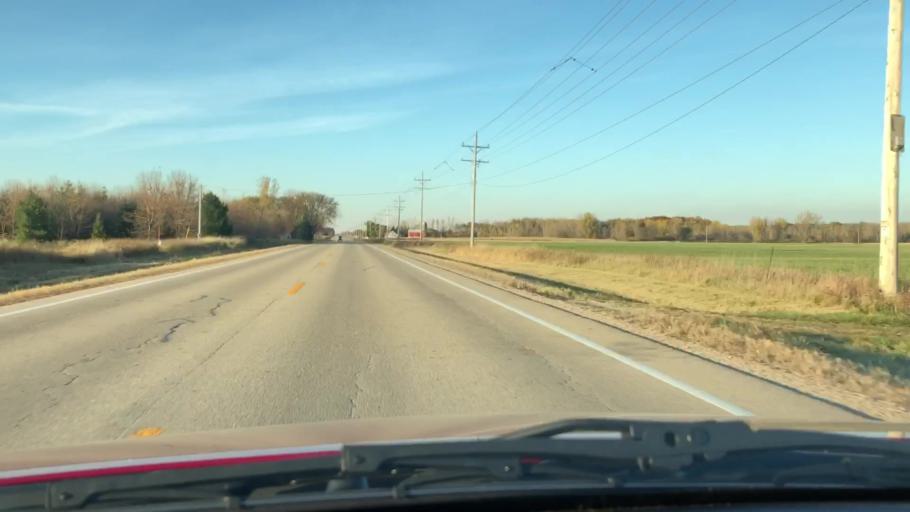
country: US
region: Wisconsin
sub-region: Outagamie County
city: Seymour
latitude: 44.4691
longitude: -88.2911
